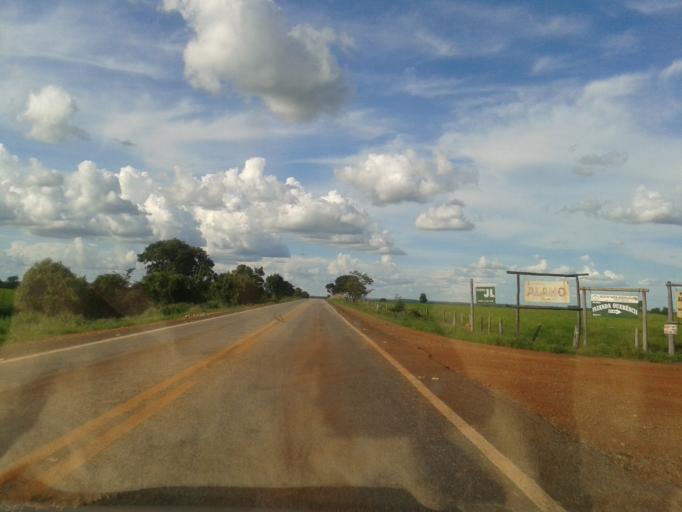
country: BR
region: Goias
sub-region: Mozarlandia
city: Mozarlandia
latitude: -14.5288
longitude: -50.4860
